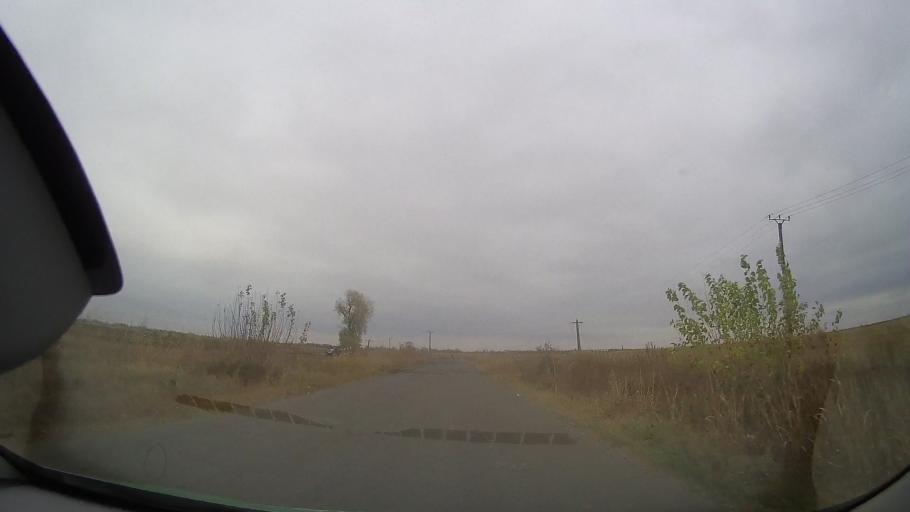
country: RO
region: Braila
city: Dudesti
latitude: 44.9332
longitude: 27.4269
